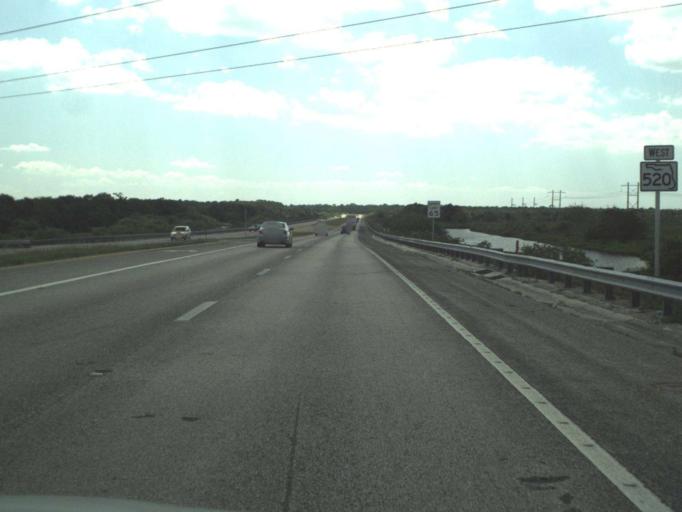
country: US
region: Florida
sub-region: Brevard County
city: Cocoa West
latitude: 28.3698
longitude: -80.8752
